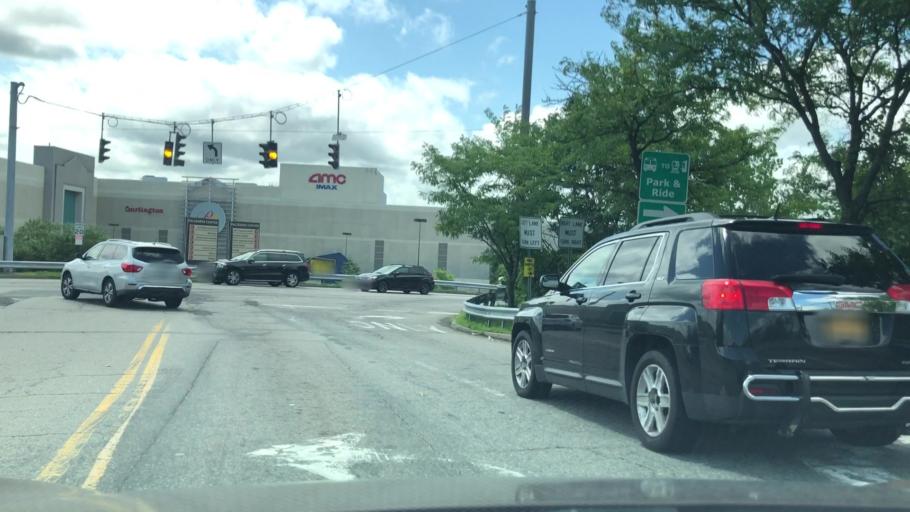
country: US
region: New York
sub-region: Rockland County
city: West Nyack
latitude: 41.1002
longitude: -73.9568
